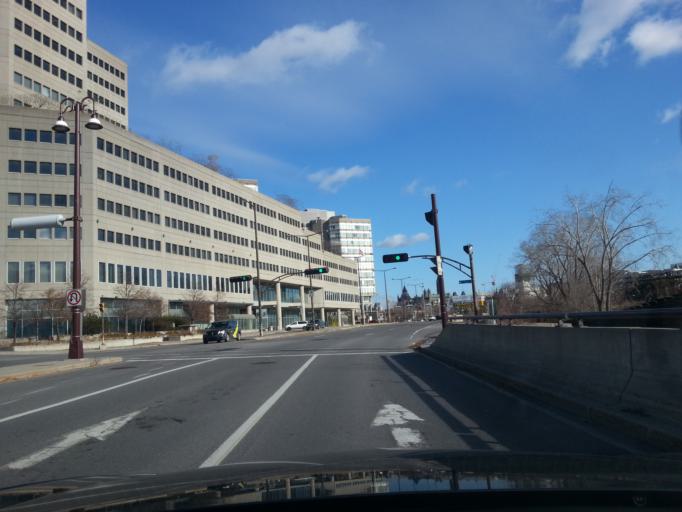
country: CA
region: Ontario
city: Ottawa
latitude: 45.4246
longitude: -75.7170
